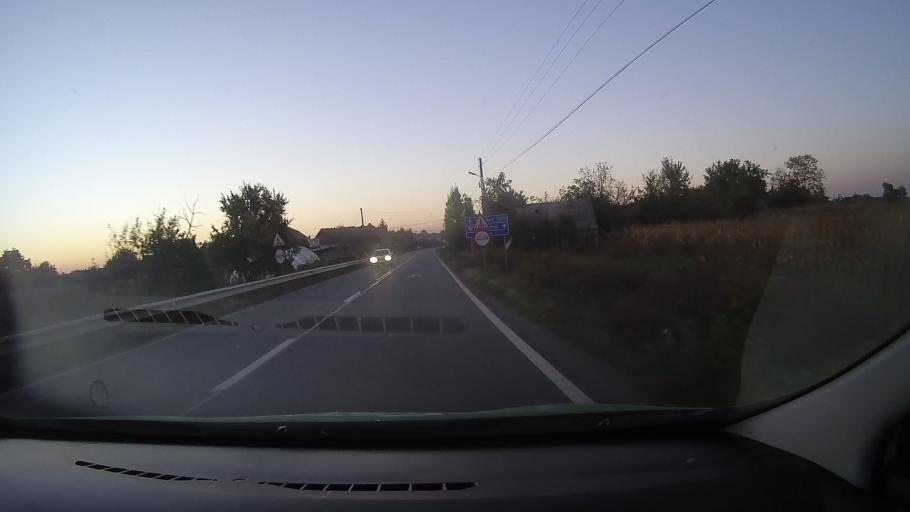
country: RO
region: Bihor
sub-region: Comuna Tarcea
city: Tarcea
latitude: 47.4559
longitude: 22.1748
